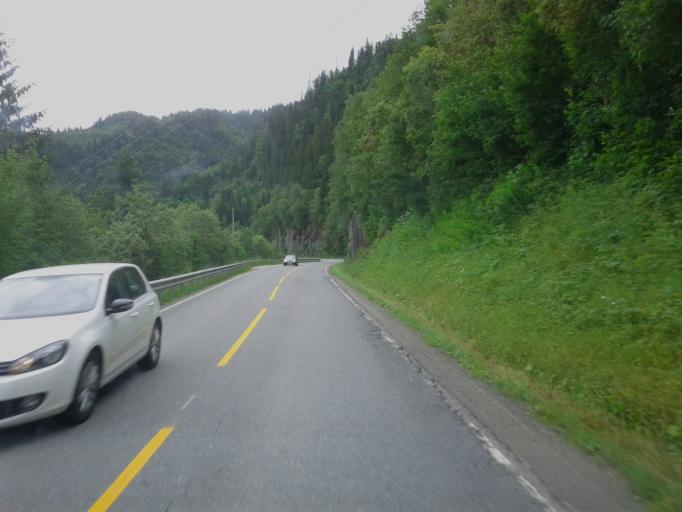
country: NO
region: Sor-Trondelag
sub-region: Midtre Gauldal
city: Storen
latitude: 62.9963
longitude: 10.4669
